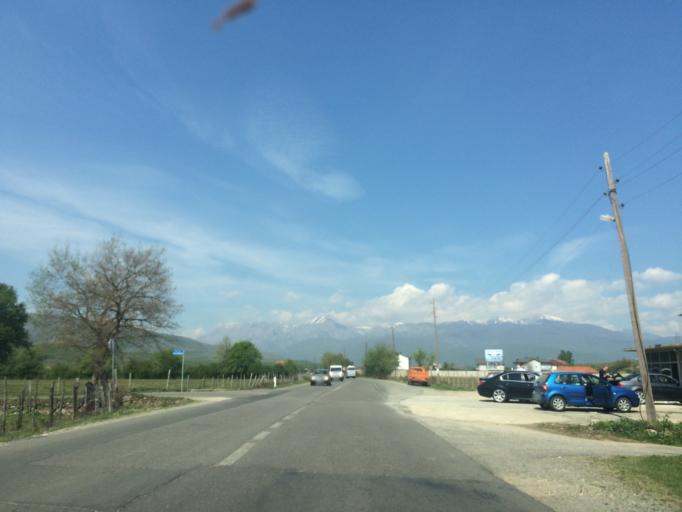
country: XK
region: Gjakova
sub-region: Komuna e Gjakoves
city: Gjakove
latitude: 42.3762
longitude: 20.3345
